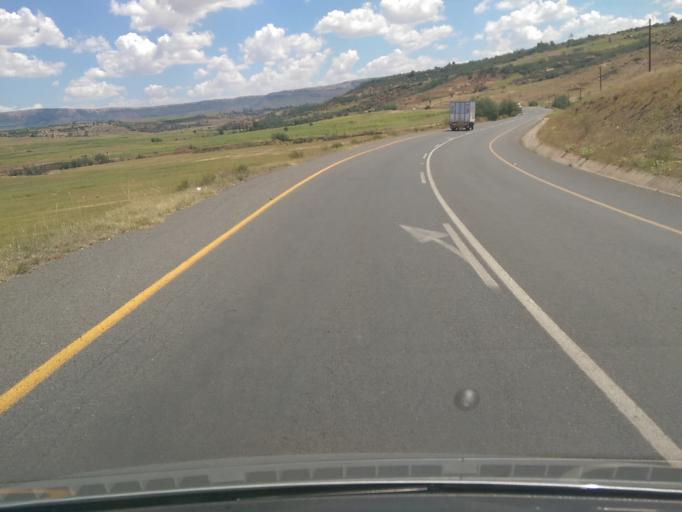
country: LS
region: Maseru
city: Maseru
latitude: -29.3923
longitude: 27.5468
